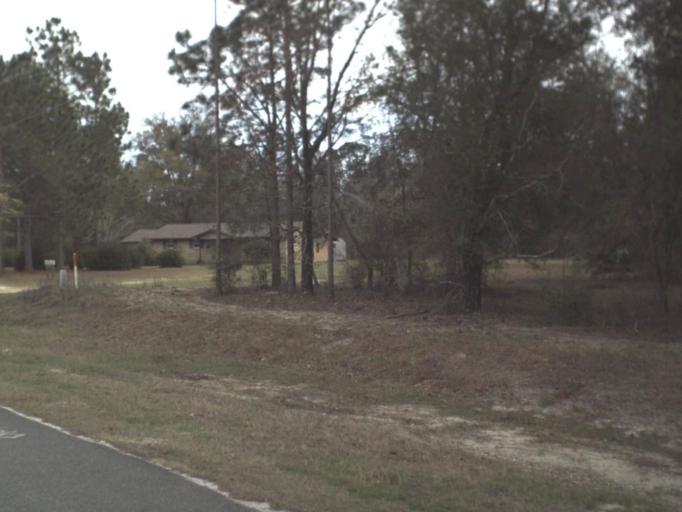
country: US
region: Florida
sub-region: Wakulla County
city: Crawfordville
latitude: 30.2620
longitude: -84.3599
